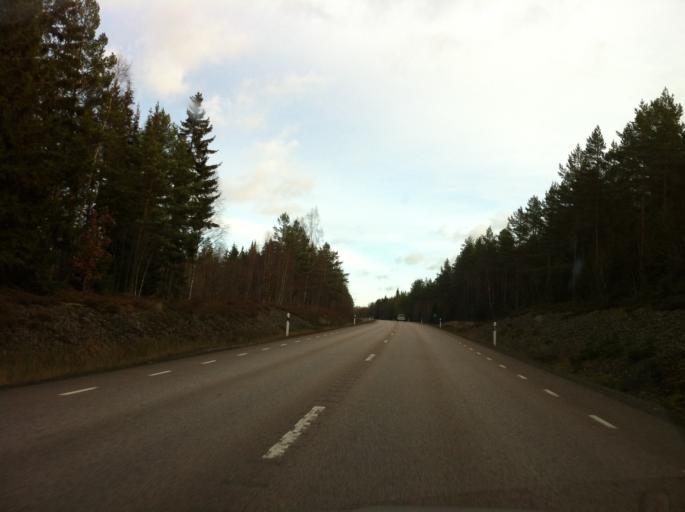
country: SE
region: Kronoberg
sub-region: Uppvidinge Kommun
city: Aseda
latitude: 57.1558
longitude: 15.3207
